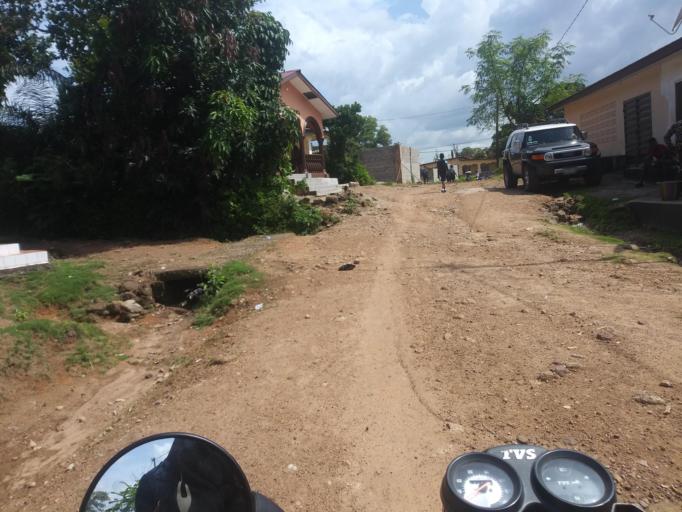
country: SL
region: Northern Province
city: Makeni
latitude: 8.8772
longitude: -12.0342
